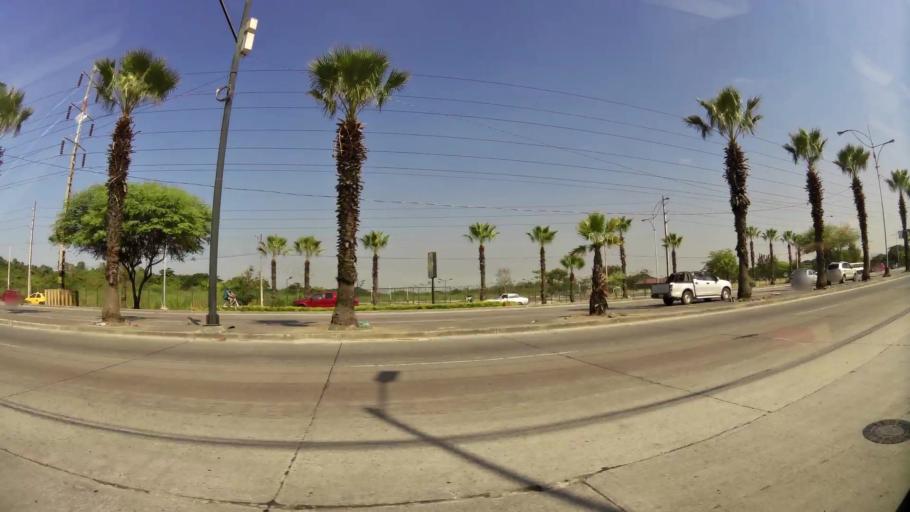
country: EC
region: Guayas
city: Eloy Alfaro
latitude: -2.1037
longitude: -79.9095
